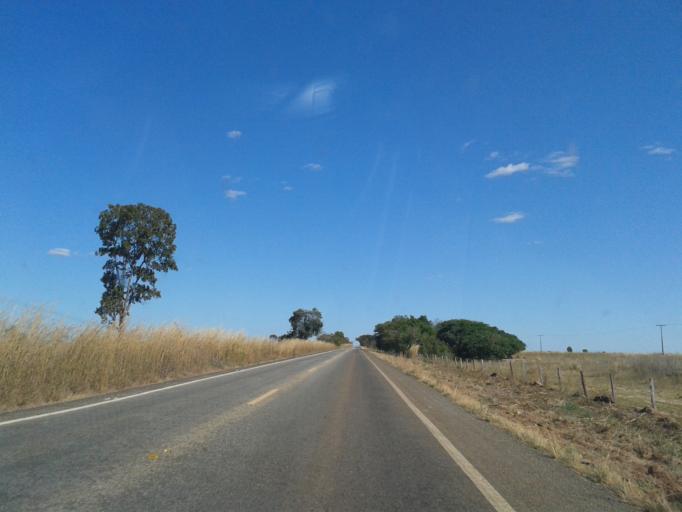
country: BR
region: Goias
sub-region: Mozarlandia
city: Mozarlandia
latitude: -14.5119
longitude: -50.4852
